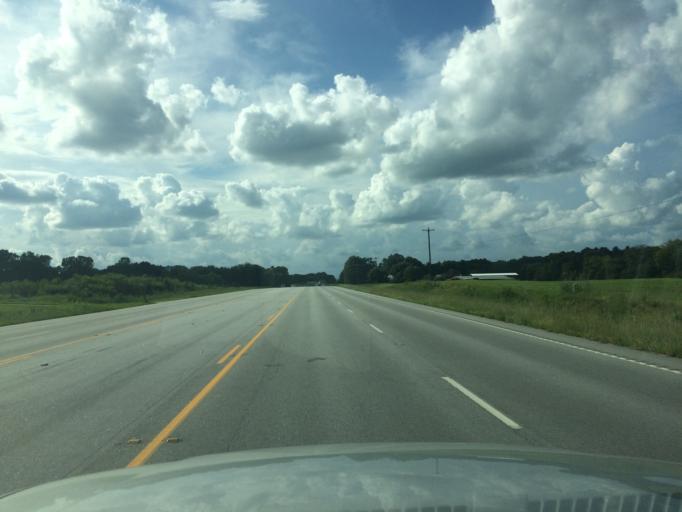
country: US
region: South Carolina
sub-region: Greenville County
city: Five Forks
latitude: 34.8047
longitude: -82.1263
